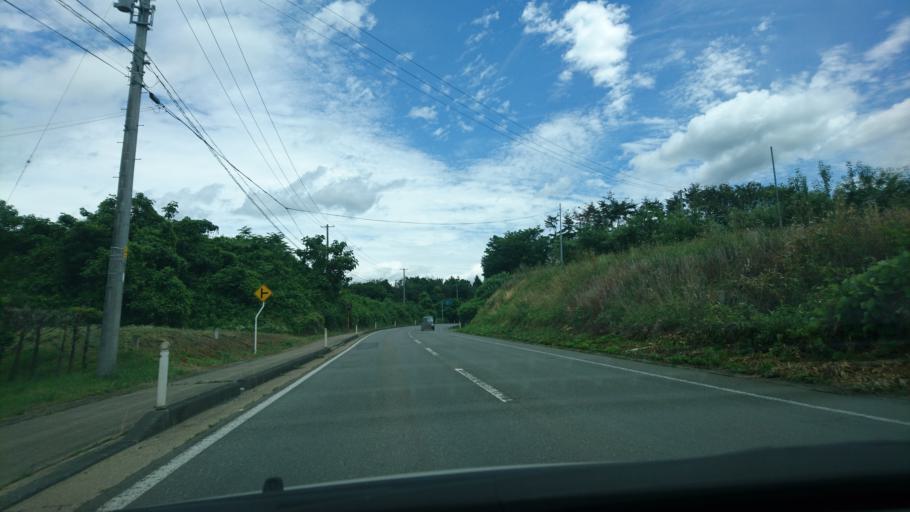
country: JP
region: Iwate
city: Morioka-shi
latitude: 39.6000
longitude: 141.2027
